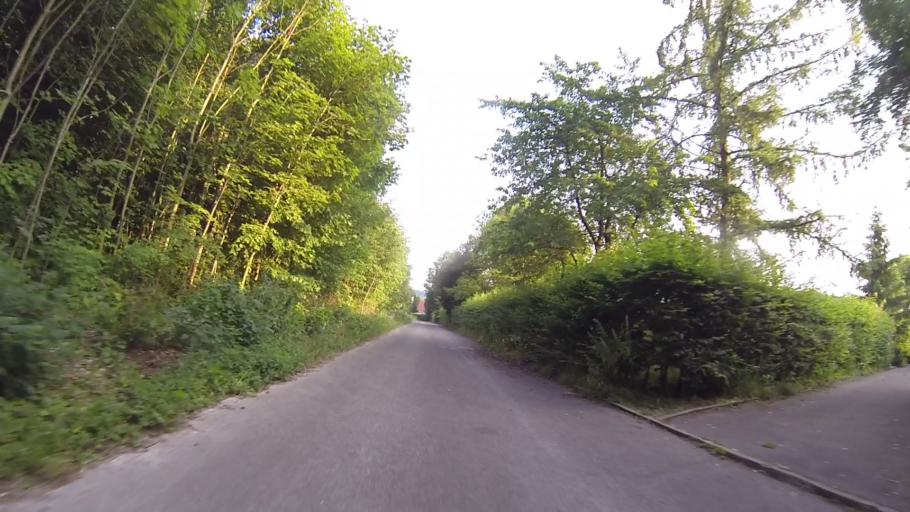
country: DE
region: Baden-Wuerttemberg
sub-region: Tuebingen Region
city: Dornstadt
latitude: 48.4254
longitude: 9.8880
